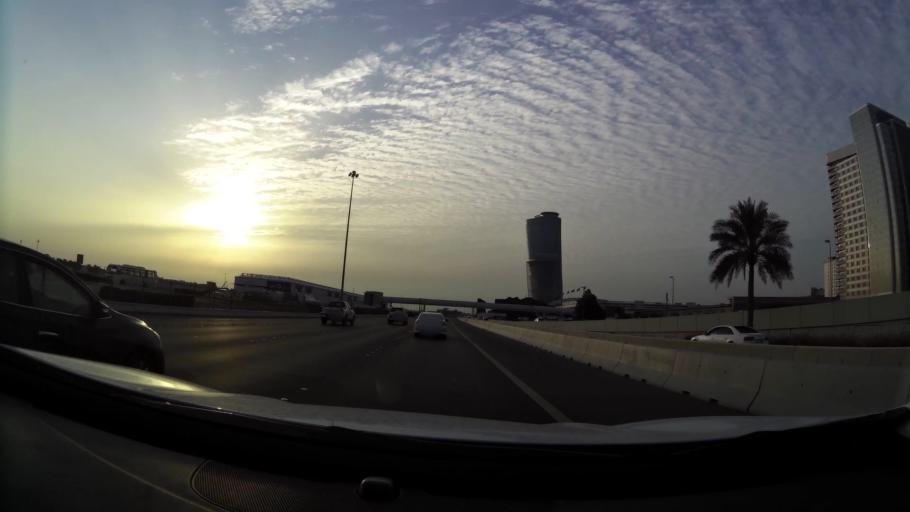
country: AE
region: Abu Dhabi
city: Abu Dhabi
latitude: 24.4160
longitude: 54.4407
